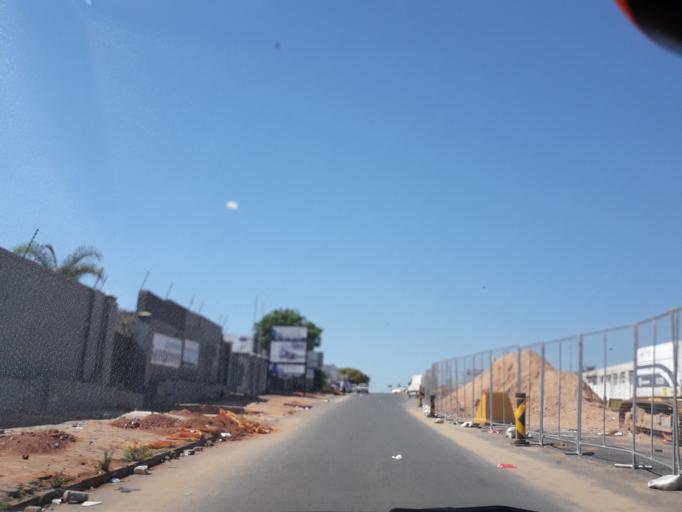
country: ZA
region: Gauteng
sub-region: City of Johannesburg Metropolitan Municipality
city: Modderfontein
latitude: -26.1119
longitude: 28.0848
